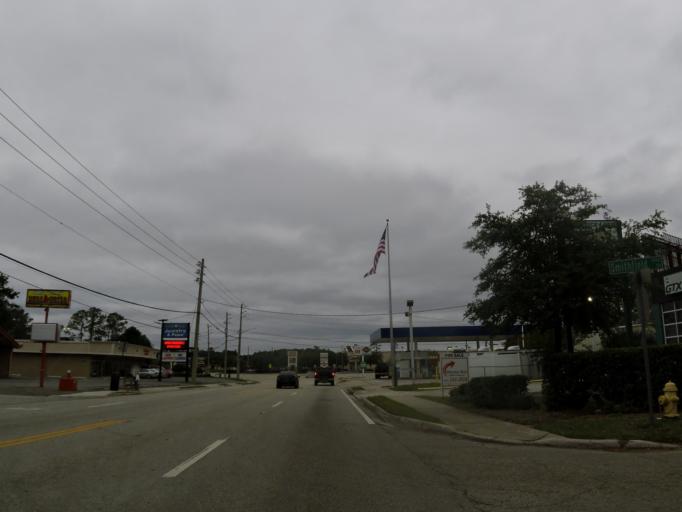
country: US
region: Florida
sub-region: Duval County
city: Jacksonville
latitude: 30.2587
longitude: -81.6260
